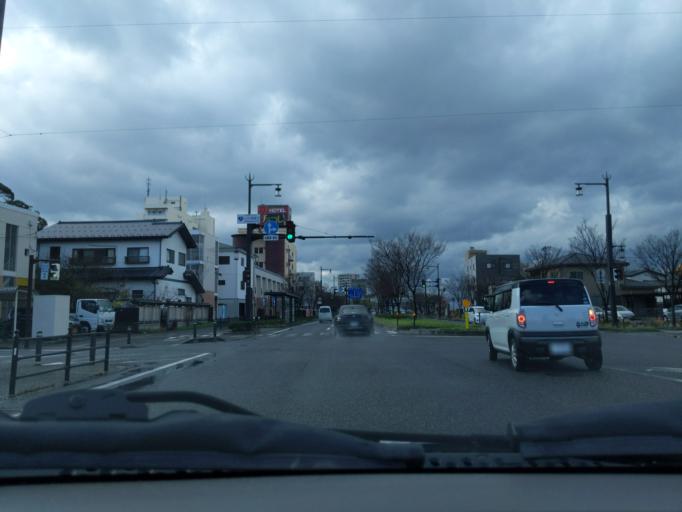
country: JP
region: Niigata
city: Niigata-shi
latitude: 37.9255
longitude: 139.0495
